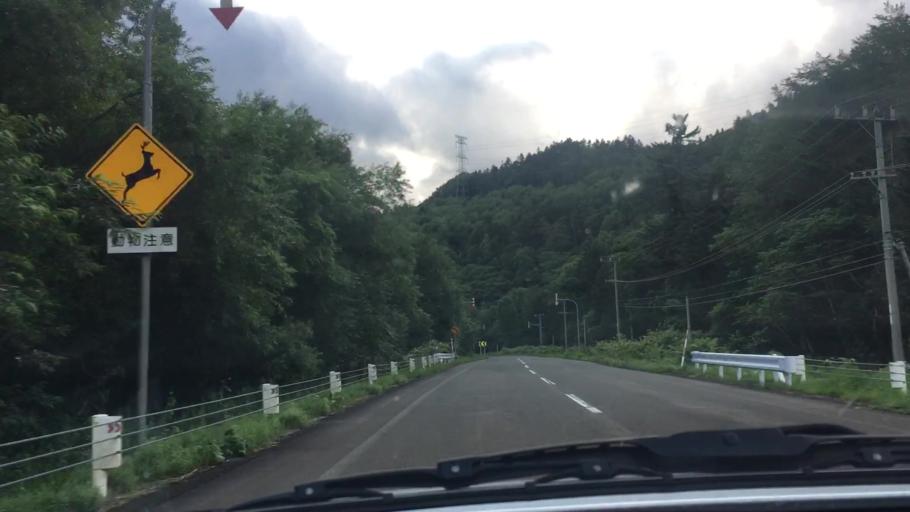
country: JP
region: Hokkaido
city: Shimo-furano
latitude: 43.0538
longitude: 142.4912
